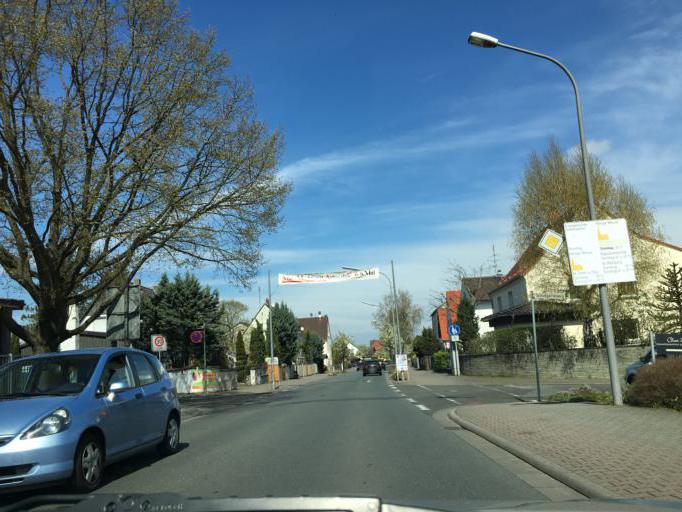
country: DE
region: Hesse
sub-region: Regierungsbezirk Darmstadt
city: Gross-Zimmern
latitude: 49.8898
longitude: 8.8315
